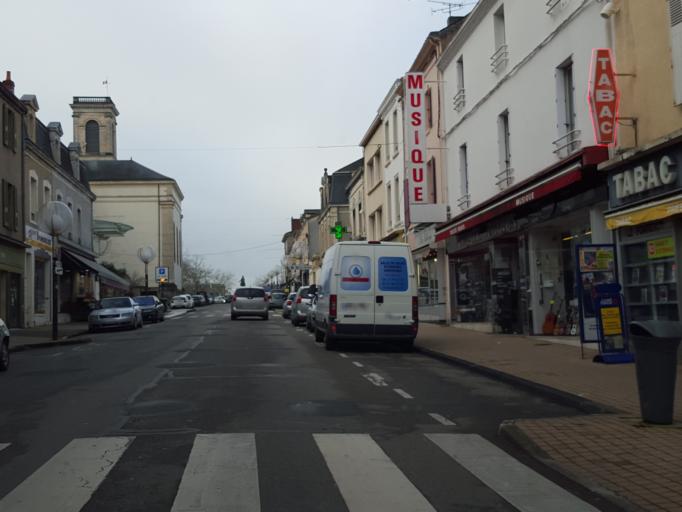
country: FR
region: Pays de la Loire
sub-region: Departement de la Vendee
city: La Roche-sur-Yon
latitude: 46.6714
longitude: -1.4235
